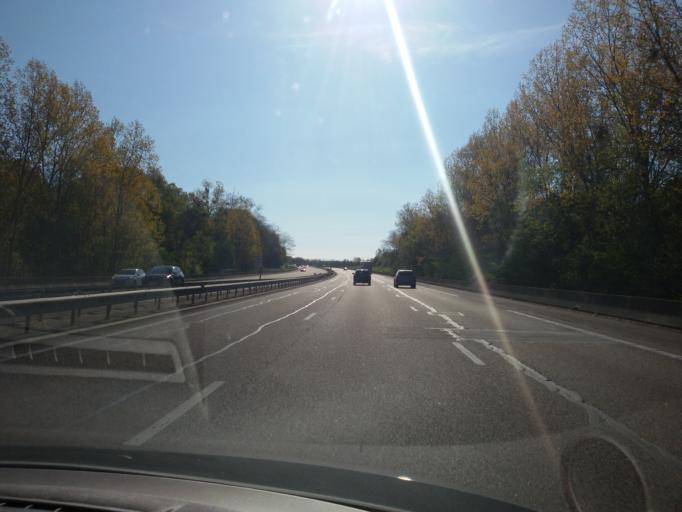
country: FR
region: Bourgogne
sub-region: Departement de l'Yonne
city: Fleury-la-Vallee
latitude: 47.8800
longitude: 3.4429
